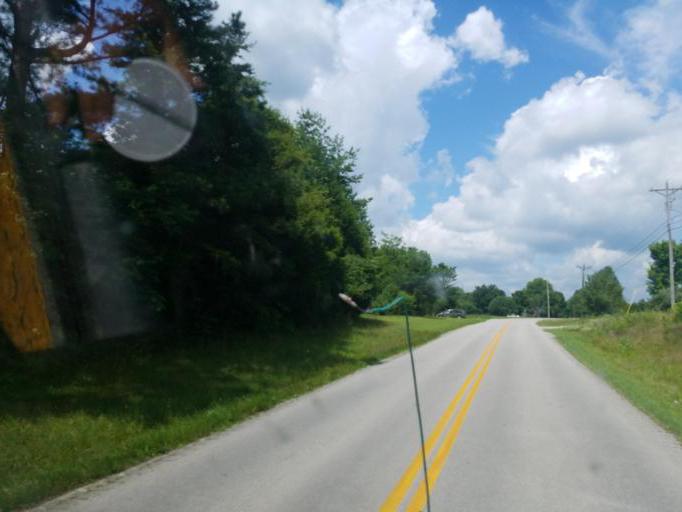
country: US
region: Kentucky
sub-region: Grayson County
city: Leitchfield
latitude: 37.5071
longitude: -86.3200
